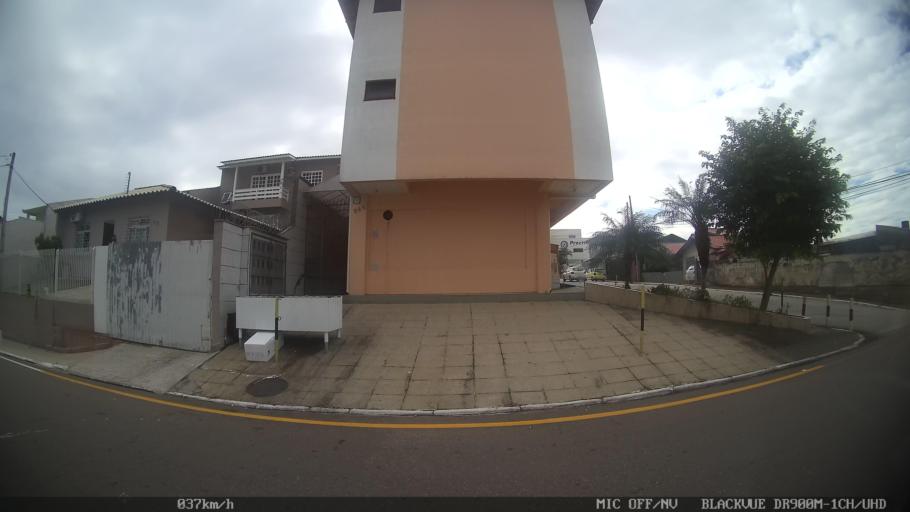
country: BR
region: Santa Catarina
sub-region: Sao Jose
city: Campinas
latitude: -27.5740
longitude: -48.6158
